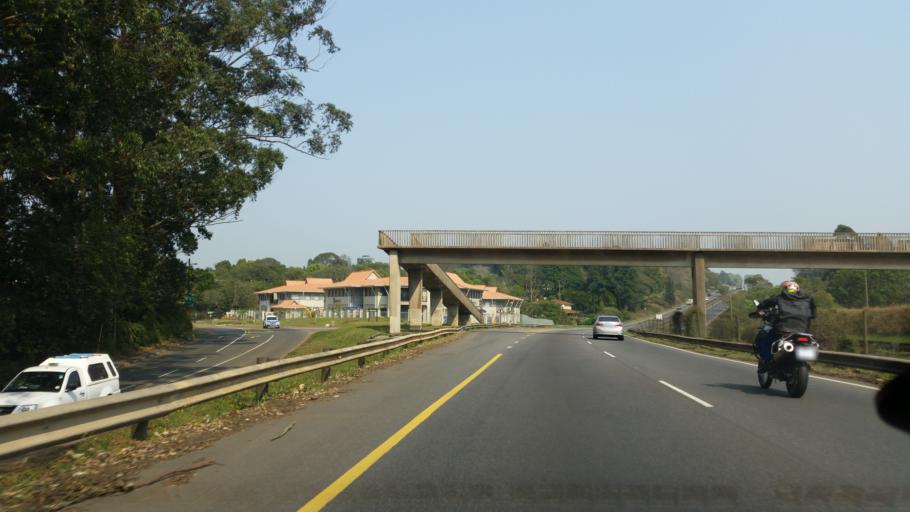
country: ZA
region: KwaZulu-Natal
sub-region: eThekwini Metropolitan Municipality
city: Mpumalanga
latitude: -29.7940
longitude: 30.7989
